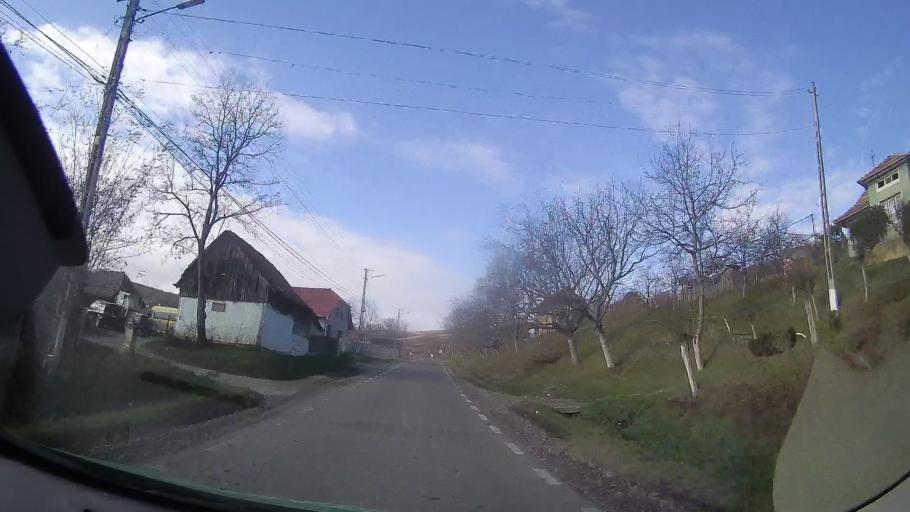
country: RO
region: Mures
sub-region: Comuna Papiu Ilarian
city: Papiu Ilarian
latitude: 46.5584
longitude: 24.1886
